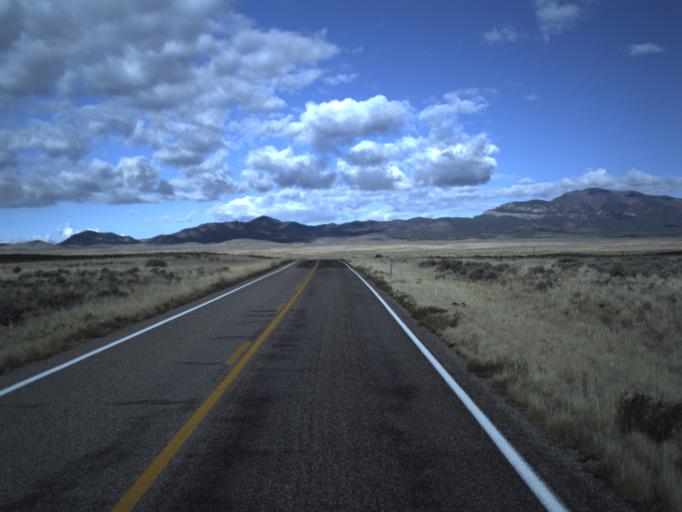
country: US
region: Utah
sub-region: Beaver County
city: Milford
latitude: 38.4371
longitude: -113.1451
